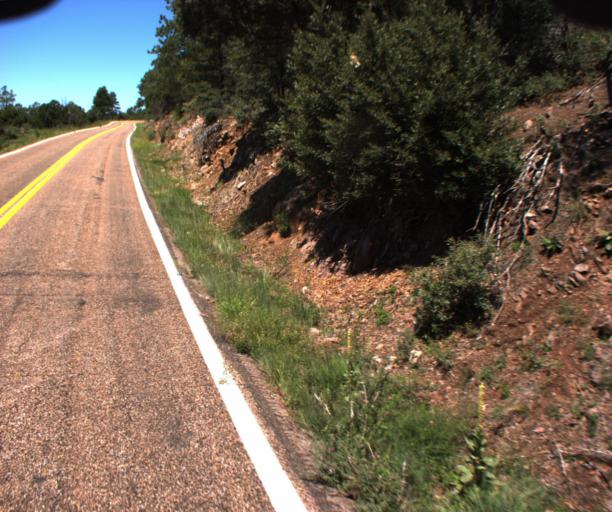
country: US
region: Arizona
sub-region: Greenlee County
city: Morenci
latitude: 33.4845
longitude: -109.3588
